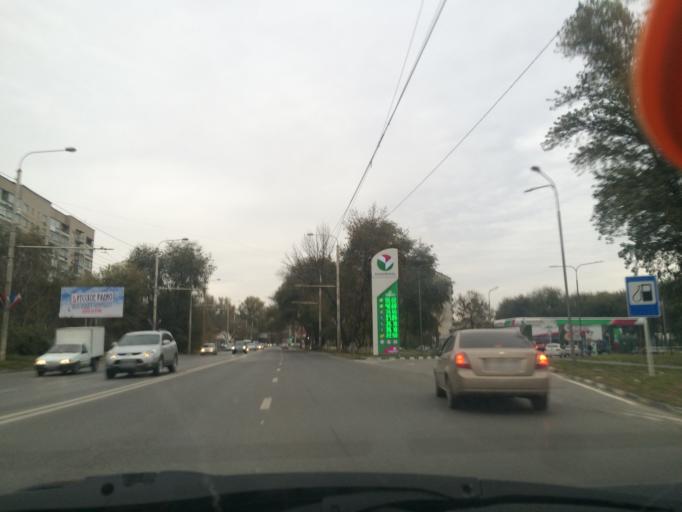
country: RU
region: Rostov
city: Severnyy
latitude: 47.2609
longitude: 39.6532
